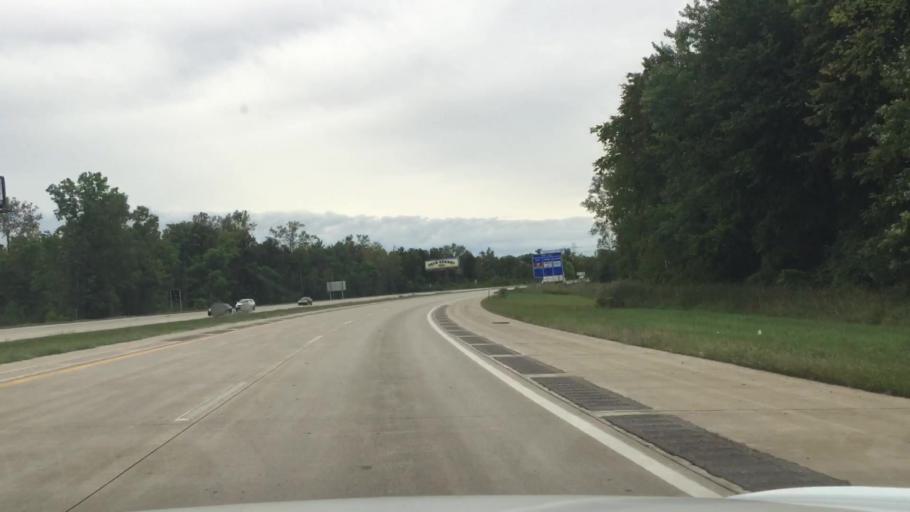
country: US
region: Michigan
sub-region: Saint Clair County
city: Marysville
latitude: 42.9575
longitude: -82.4912
